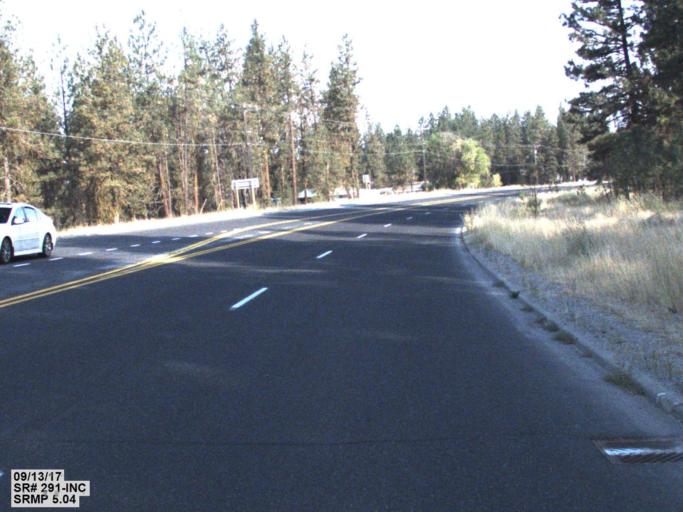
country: US
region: Washington
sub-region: Spokane County
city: Town and Country
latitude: 47.7346
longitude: -117.5070
